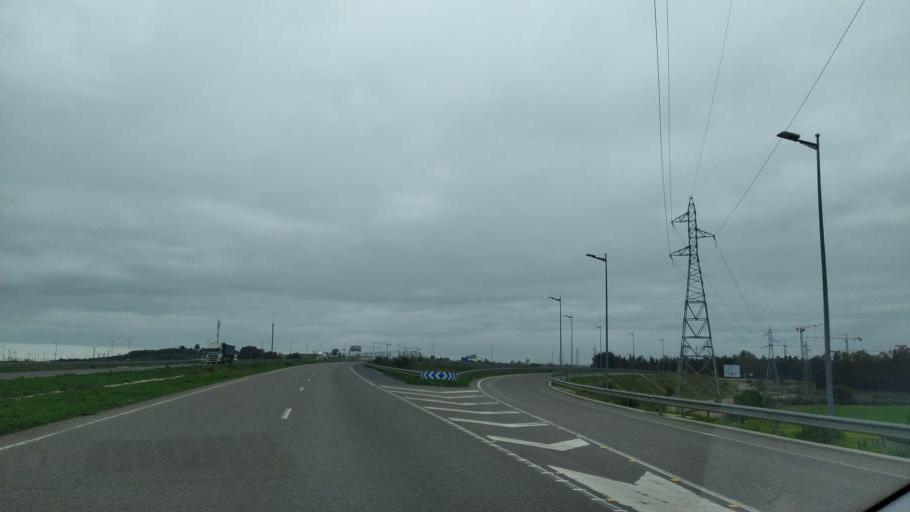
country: MA
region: Rabat-Sale-Zemmour-Zaer
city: Sale
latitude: 33.9725
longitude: -6.7383
